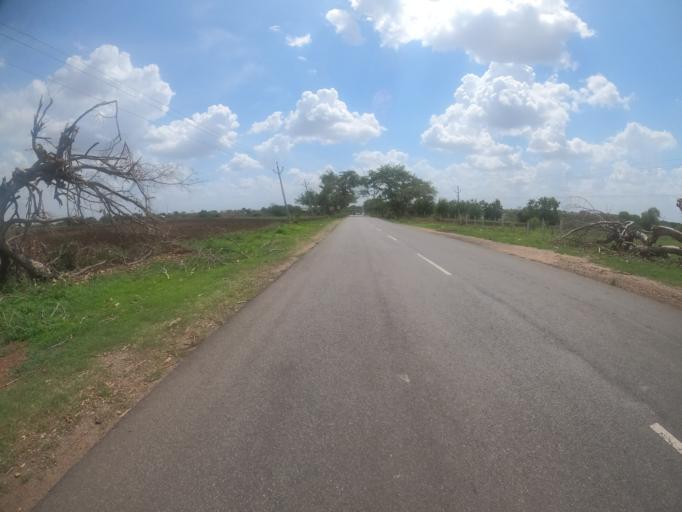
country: IN
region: Telangana
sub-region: Rangareddi
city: Sriramnagar
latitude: 17.3056
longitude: 78.1566
